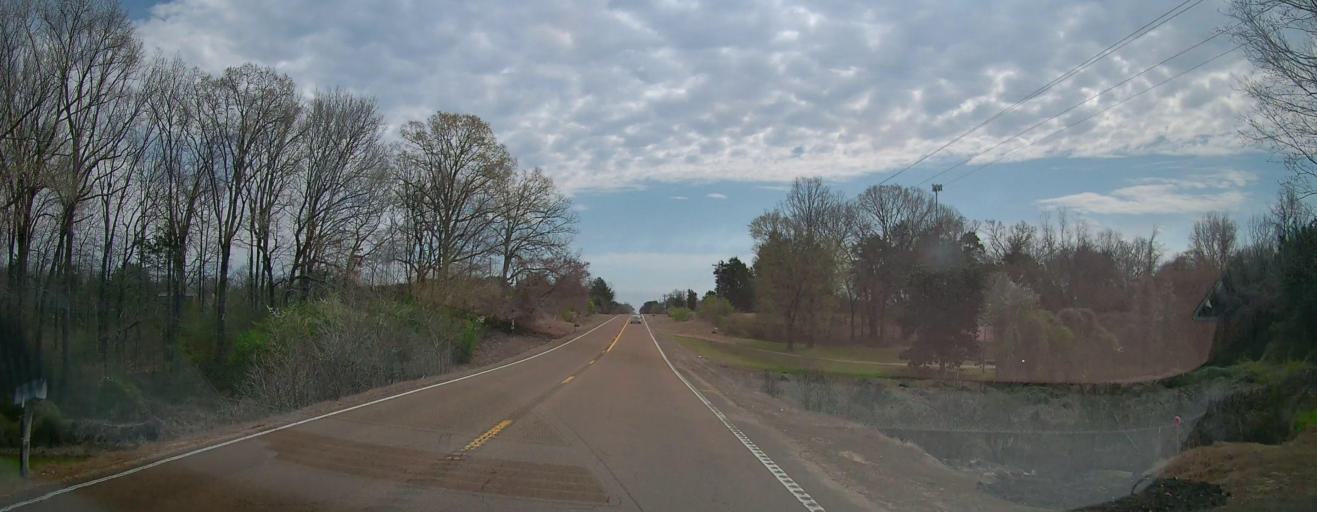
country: US
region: Mississippi
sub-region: Marshall County
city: Holly Springs
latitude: 34.8224
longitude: -89.5479
